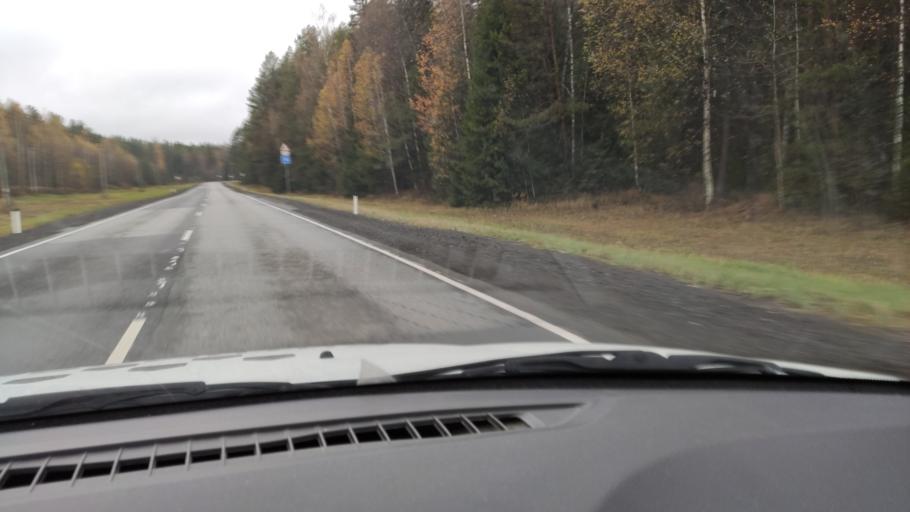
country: RU
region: Kirov
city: Belaya Kholunitsa
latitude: 58.8300
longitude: 50.6816
